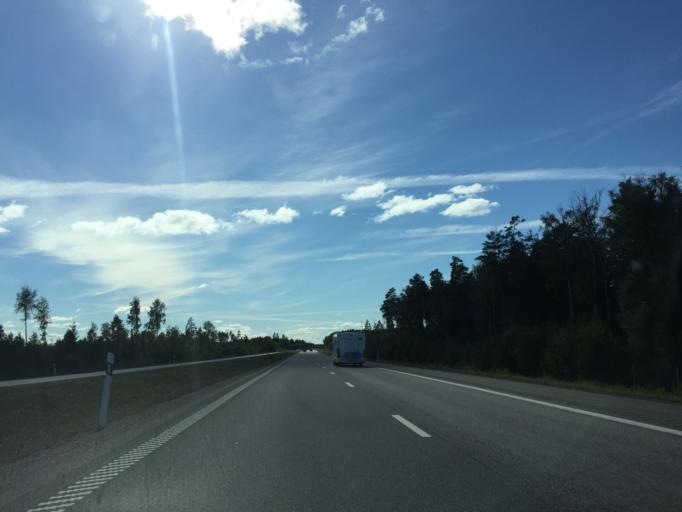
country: SE
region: OErebro
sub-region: Lindesbergs Kommun
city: Fellingsbro
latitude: 59.3513
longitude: 15.5580
